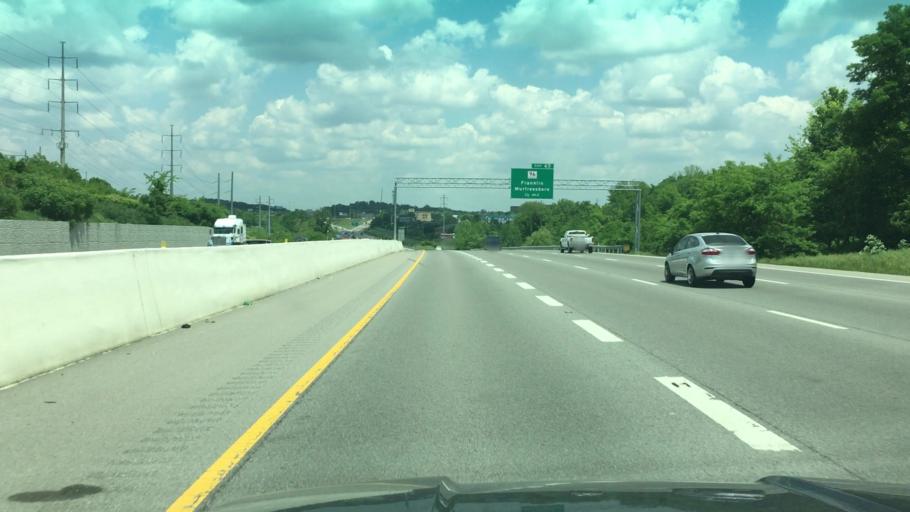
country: US
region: Tennessee
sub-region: Williamson County
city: Franklin
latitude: 35.9028
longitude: -86.8264
